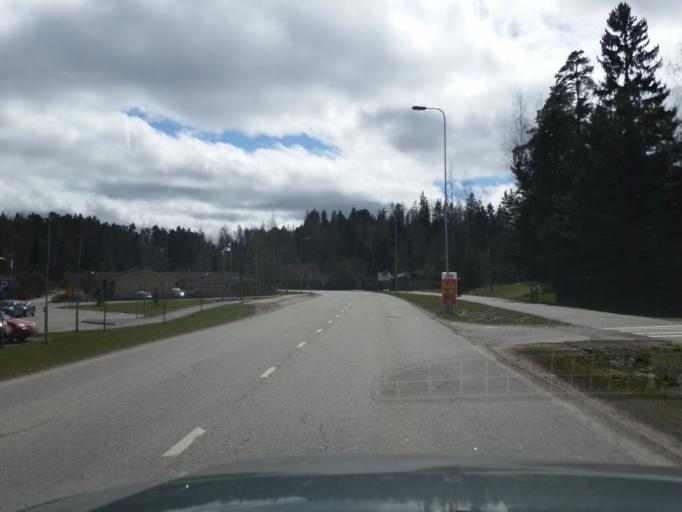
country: FI
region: Uusimaa
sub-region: Helsinki
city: Vihti
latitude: 60.4117
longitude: 24.3303
